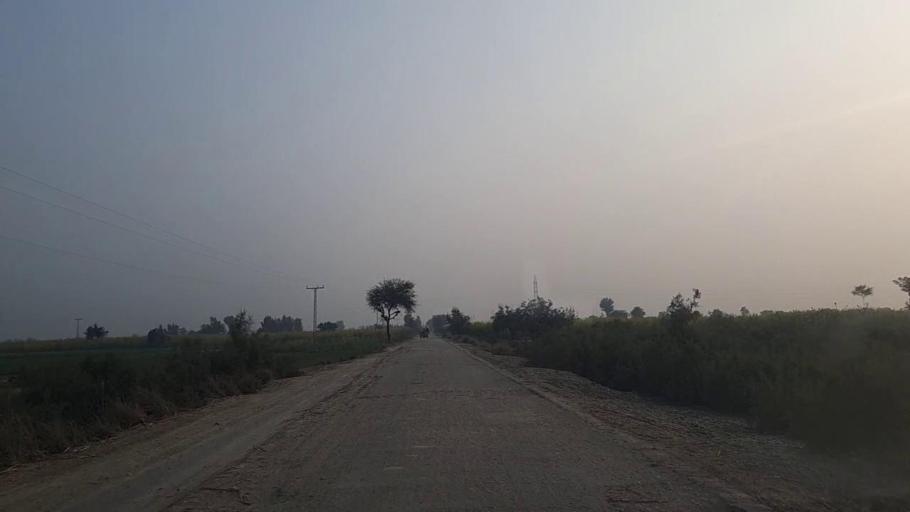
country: PK
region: Sindh
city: Khadro
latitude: 26.1160
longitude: 68.7962
